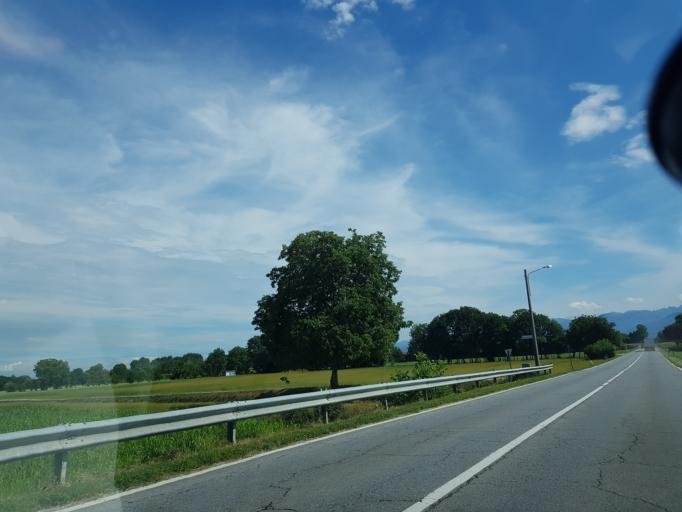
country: IT
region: Piedmont
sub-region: Provincia di Cuneo
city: Roata Rossi
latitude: 44.4529
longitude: 7.5237
